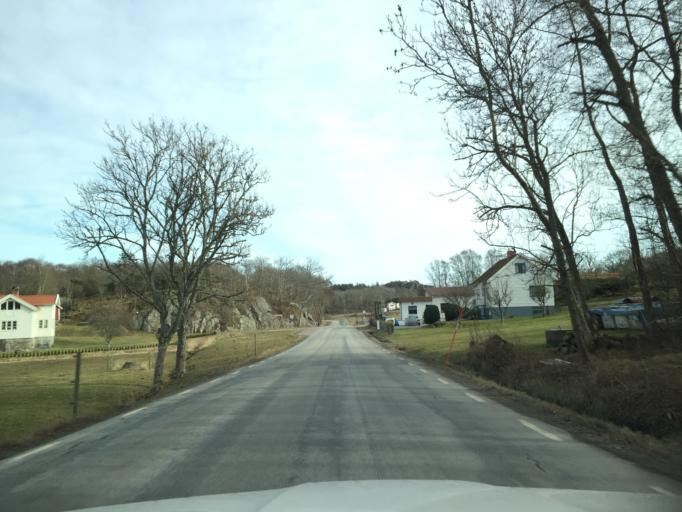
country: SE
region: Vaestra Goetaland
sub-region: Tjorns Kommun
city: Skaerhamn
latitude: 58.0361
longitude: 11.5631
